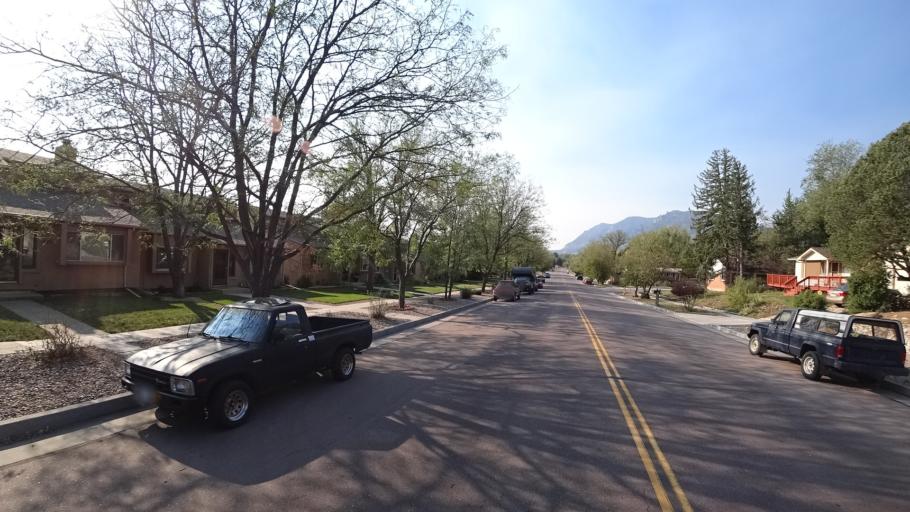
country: US
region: Colorado
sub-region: El Paso County
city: Colorado Springs
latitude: 38.8111
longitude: -104.8460
